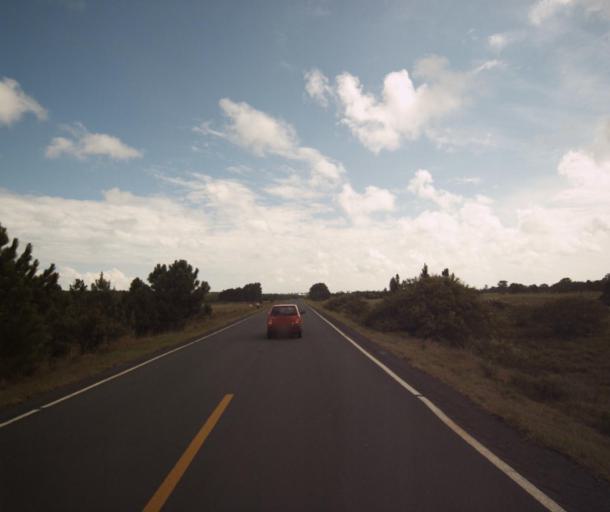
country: BR
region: Rio Grande do Sul
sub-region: Sao Lourenco Do Sul
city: Sao Lourenco do Sul
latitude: -31.4374
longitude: -51.1959
